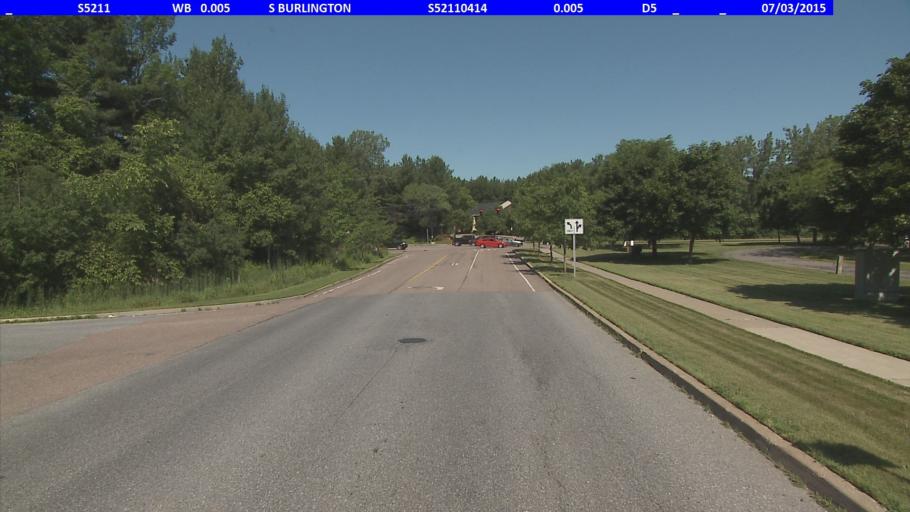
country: US
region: Vermont
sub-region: Chittenden County
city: South Burlington
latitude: 44.4600
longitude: -73.1545
